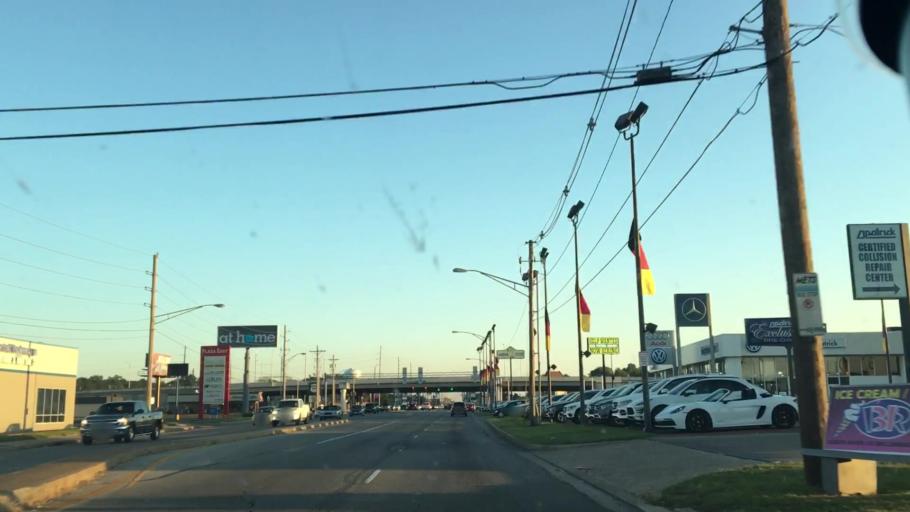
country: US
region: Indiana
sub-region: Vanderburgh County
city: Melody Hill
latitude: 37.9790
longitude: -87.4927
